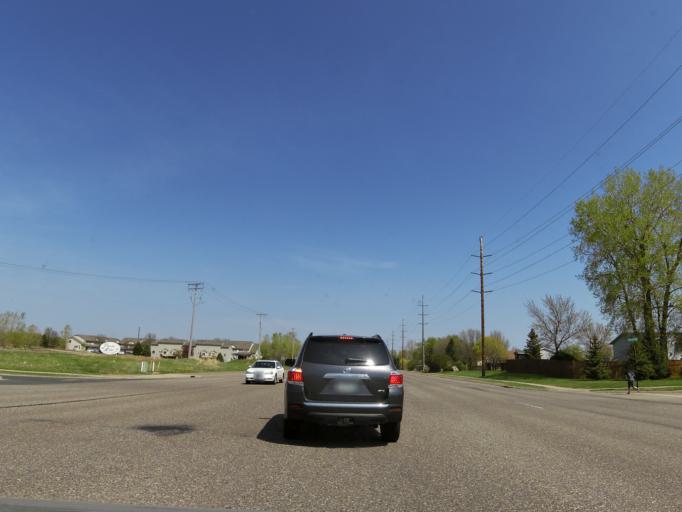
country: US
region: Minnesota
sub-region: Scott County
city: Savage
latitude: 44.7498
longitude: -93.3591
